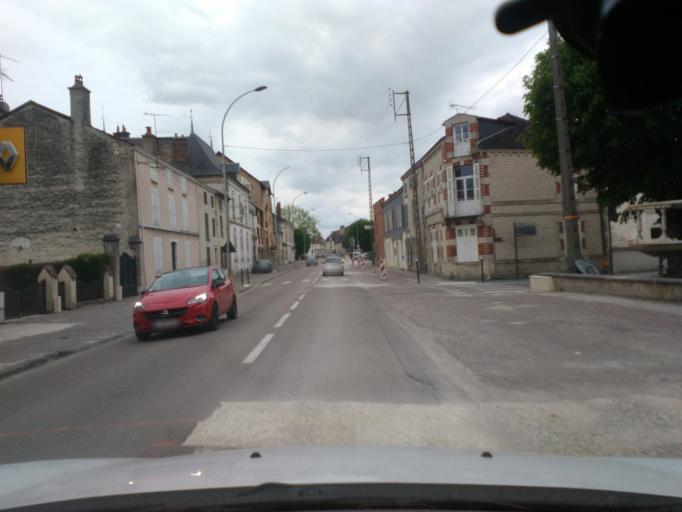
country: FR
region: Champagne-Ardenne
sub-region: Departement de l'Aube
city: Bar-sur-Aube
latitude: 48.2363
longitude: 4.7025
